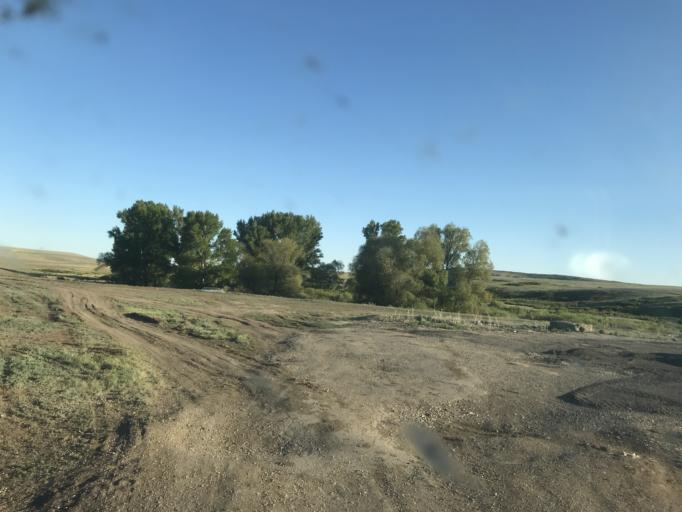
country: KZ
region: Aqtoebe
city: Aqtobe
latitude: 50.2891
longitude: 57.6799
